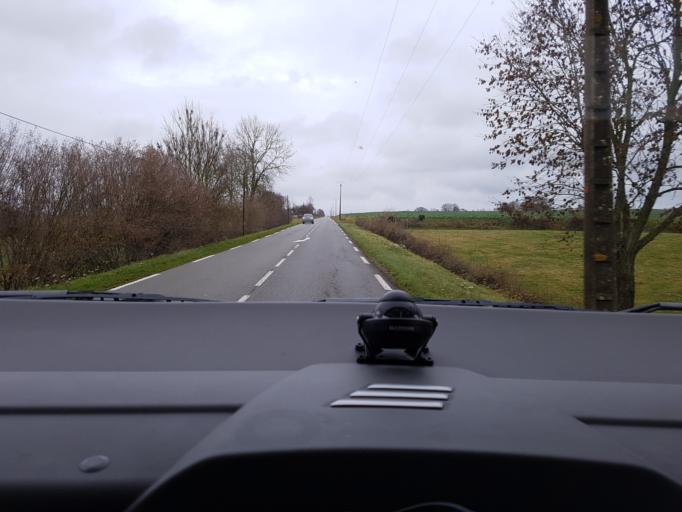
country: FR
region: Haute-Normandie
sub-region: Departement de la Seine-Maritime
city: Gournay-en-Bray
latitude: 49.4963
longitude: 1.7702
